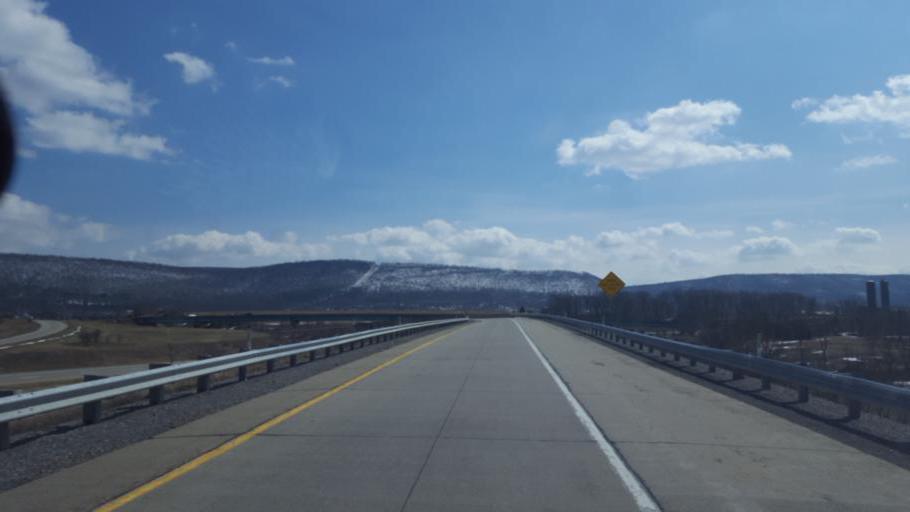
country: US
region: Pennsylvania
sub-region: Centre County
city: Pleasant Gap
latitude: 40.8922
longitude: -77.7345
